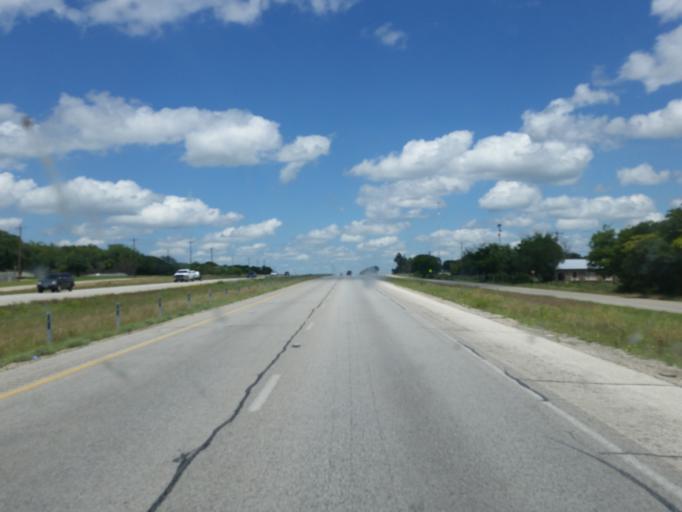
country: US
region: Texas
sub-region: Callahan County
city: Clyde
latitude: 32.4090
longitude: -99.4666
